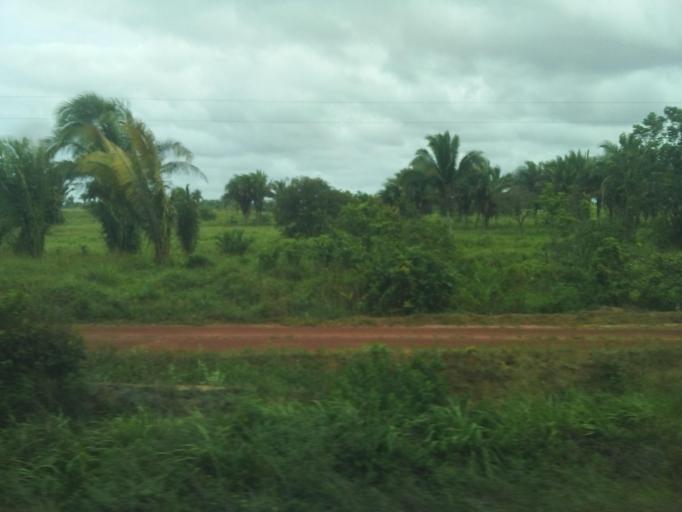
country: BR
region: Maranhao
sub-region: Itapecuru Mirim
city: Itapecuru Mirim
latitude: -3.2163
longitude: -44.4031
